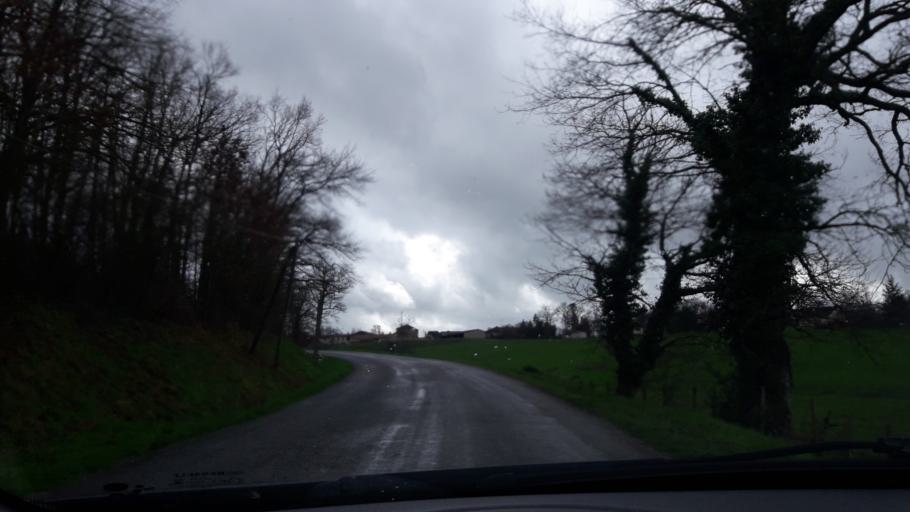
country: FR
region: Limousin
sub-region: Departement de la Haute-Vienne
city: Pierre-Buffiere
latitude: 45.7234
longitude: 1.3781
